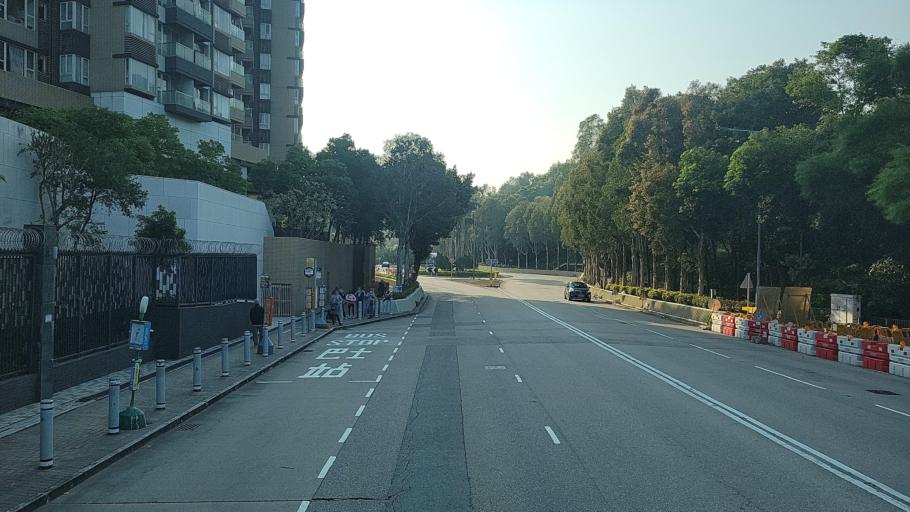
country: HK
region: Tuen Mun
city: Tuen Mun
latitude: 22.3756
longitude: 113.9998
